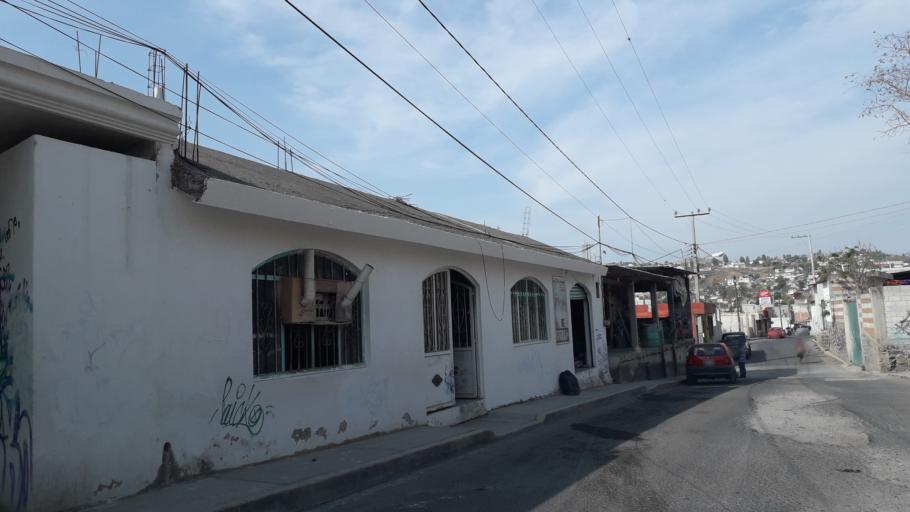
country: MX
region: Puebla
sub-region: Puebla
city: San Andres Azumiatla
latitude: 18.9042
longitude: -98.2514
